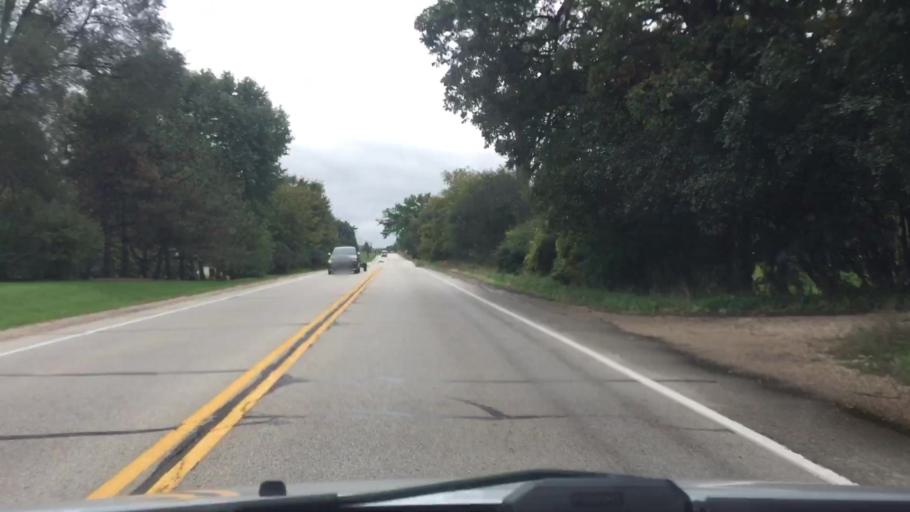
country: US
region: Wisconsin
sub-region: Walworth County
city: Elkhorn
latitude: 42.7562
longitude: -88.5538
